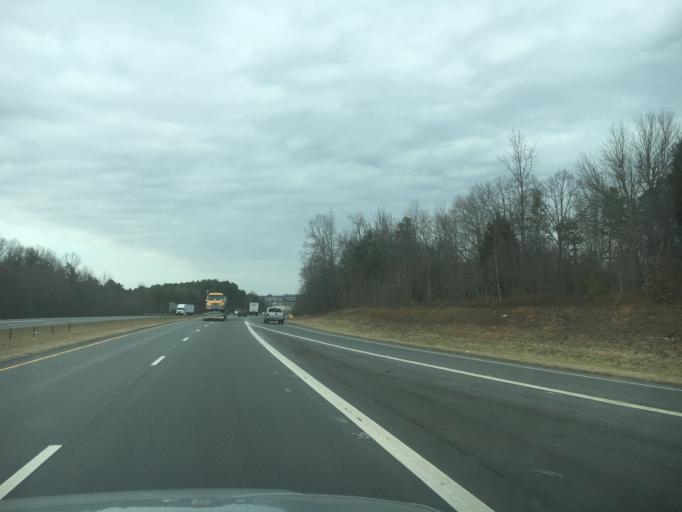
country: US
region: North Carolina
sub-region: Catawba County
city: Maiden
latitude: 35.5303
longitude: -81.2240
